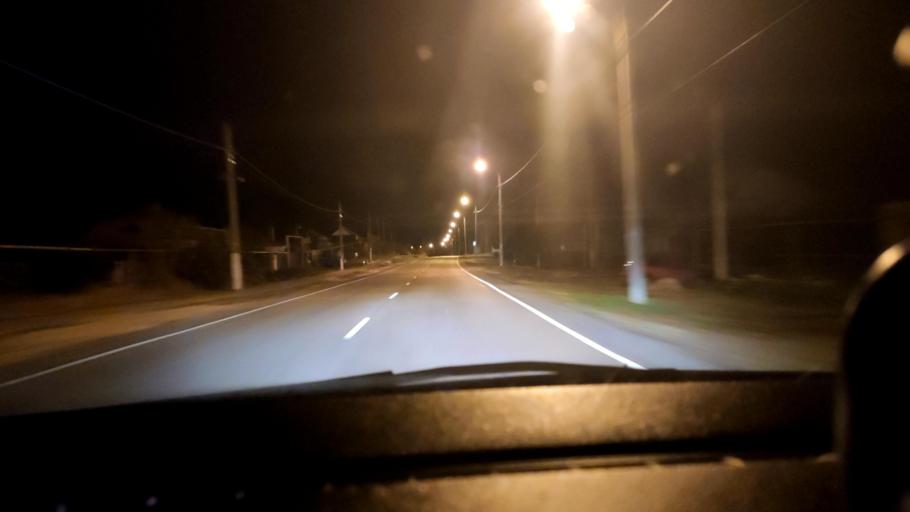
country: RU
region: Voronezj
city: Shilovo
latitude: 51.5743
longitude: 39.0405
